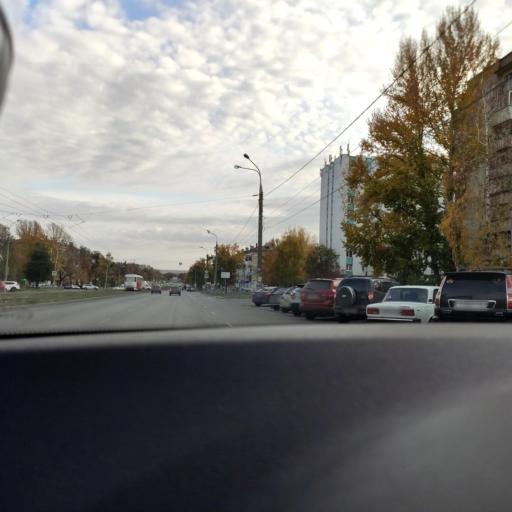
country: RU
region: Samara
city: Samara
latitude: 53.2106
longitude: 50.2299
